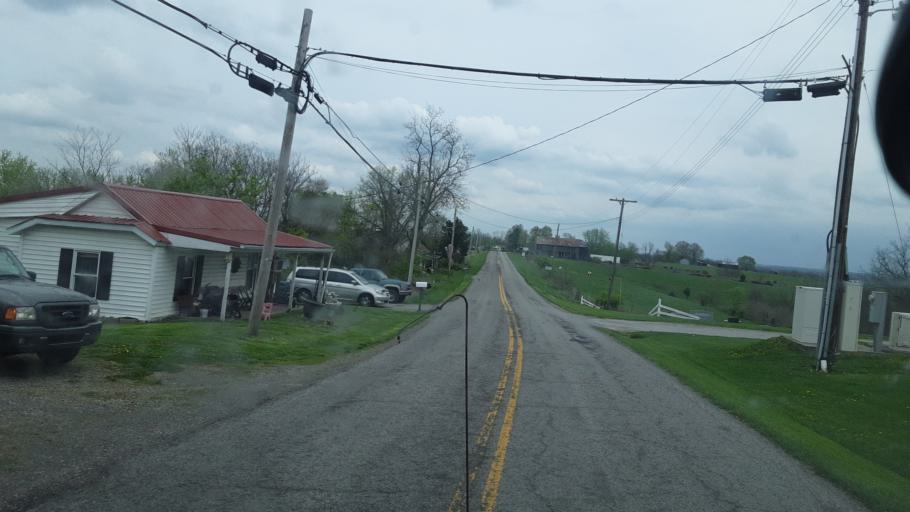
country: US
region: Kentucky
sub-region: Owen County
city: Owenton
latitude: 38.6399
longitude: -84.7719
